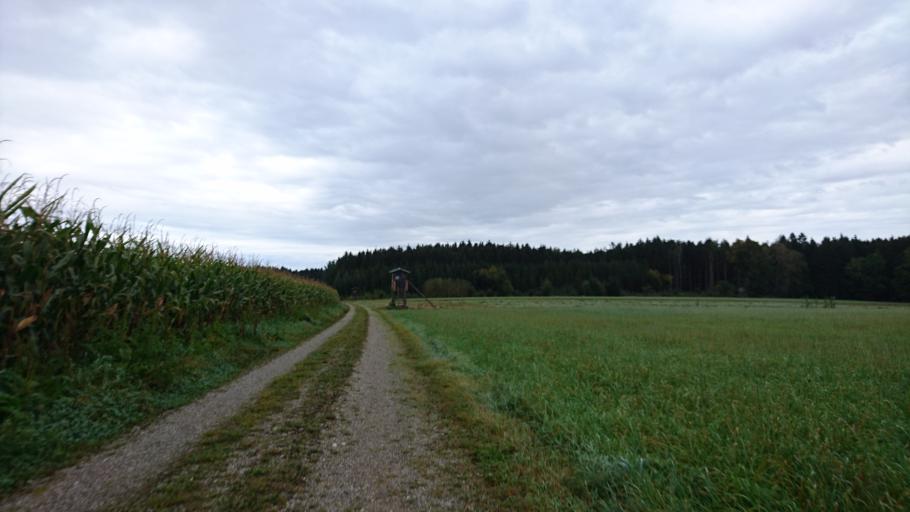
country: DE
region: Bavaria
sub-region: Swabia
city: Welden
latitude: 48.4454
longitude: 10.6440
